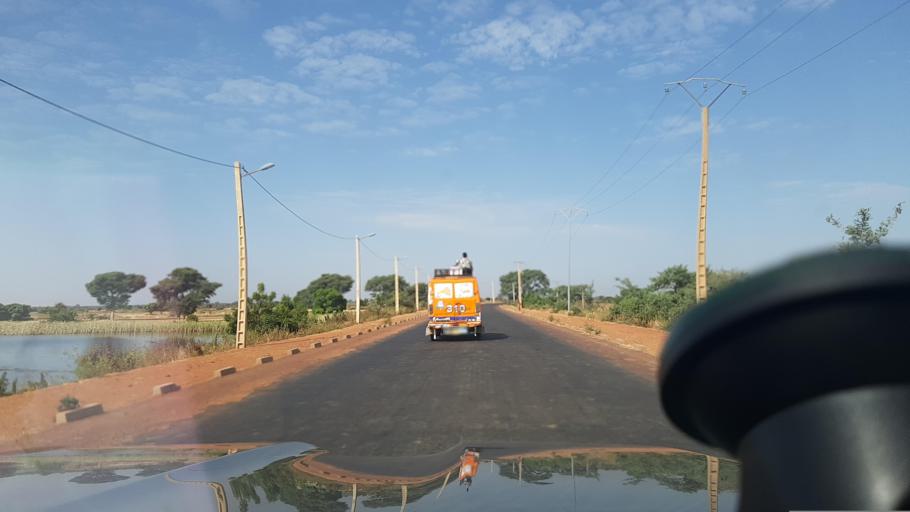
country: ML
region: Segou
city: Markala
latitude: 13.6852
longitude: -6.0964
